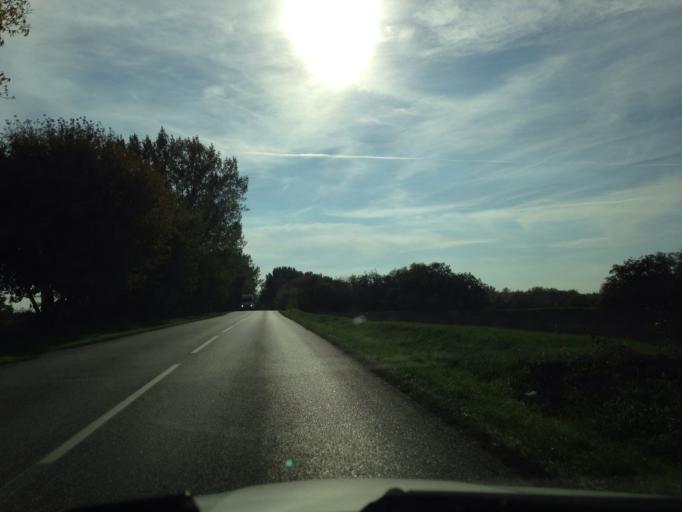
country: SK
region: Nitriansky
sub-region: Okres Komarno
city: Hurbanovo
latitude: 47.8181
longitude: 18.2251
